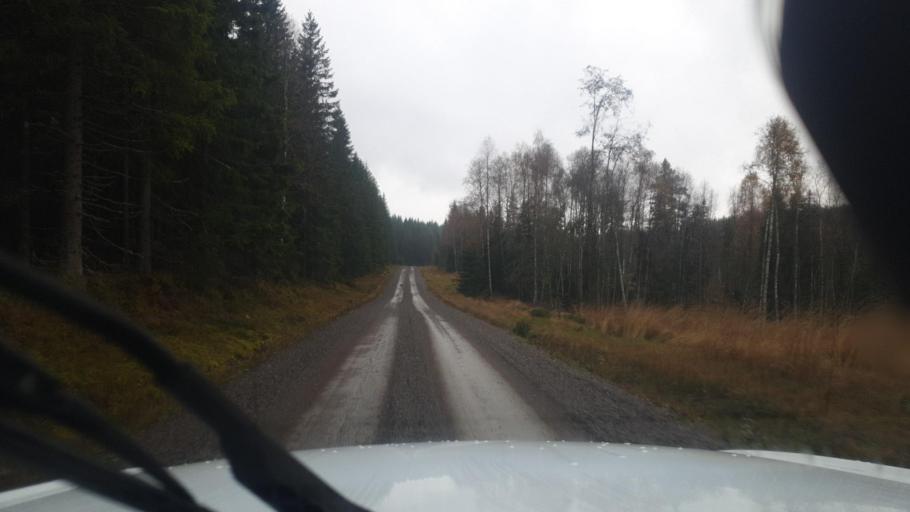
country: SE
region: Vaermland
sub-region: Eda Kommun
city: Charlottenberg
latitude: 60.0842
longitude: 12.6183
